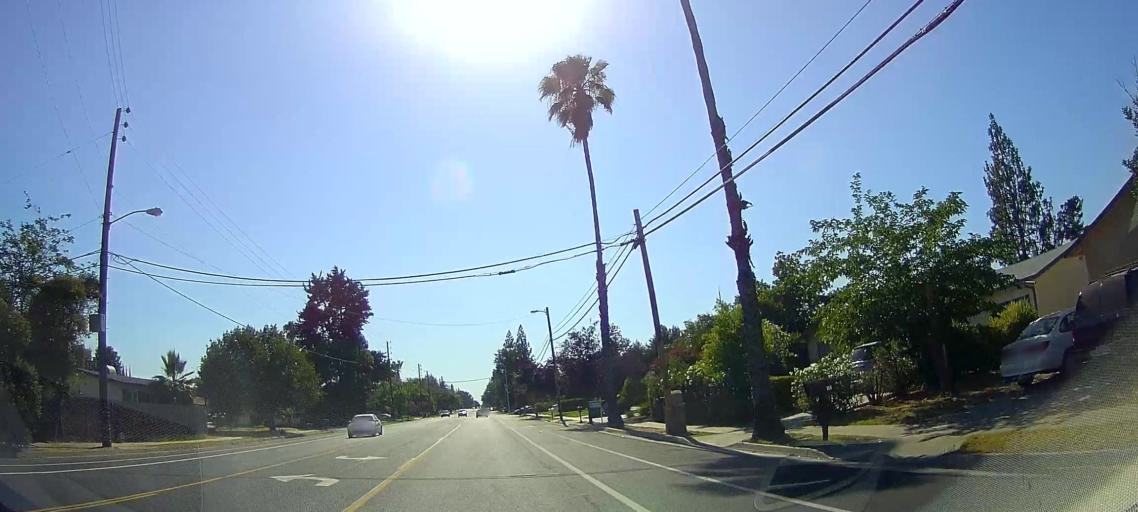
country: US
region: California
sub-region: Fresno County
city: Fresno
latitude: 36.8302
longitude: -119.7929
